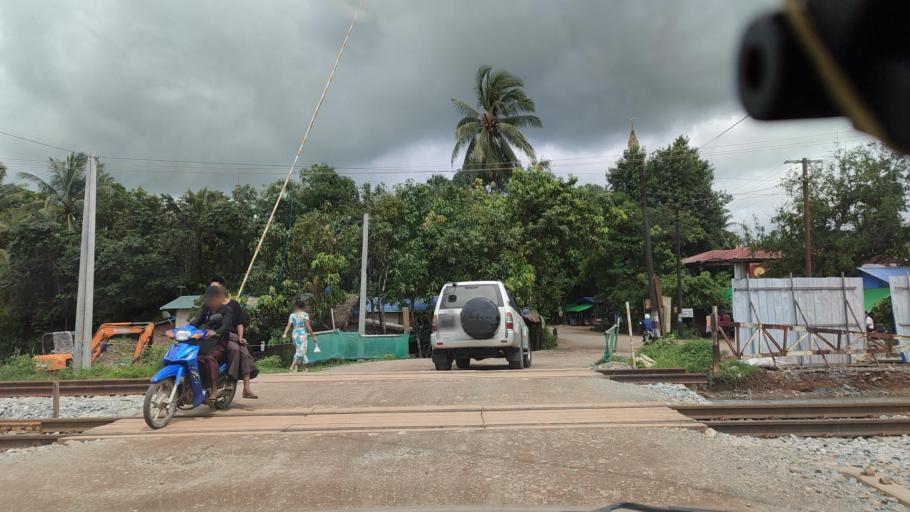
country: MM
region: Bago
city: Thanatpin
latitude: 17.1124
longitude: 96.4465
